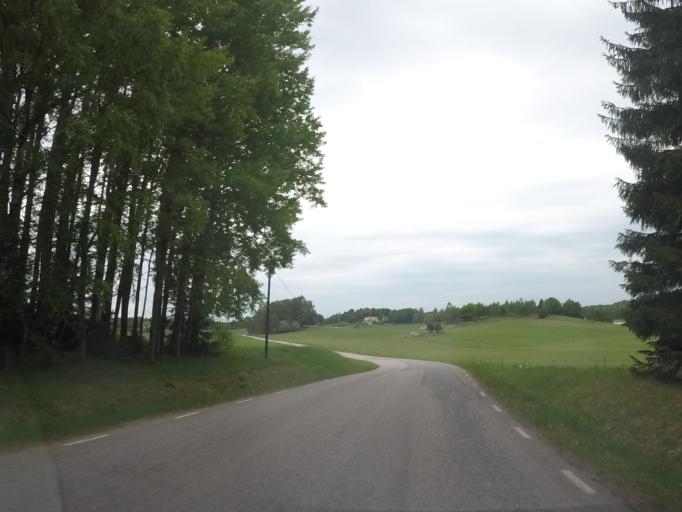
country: SE
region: Soedermanland
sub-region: Nykopings Kommun
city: Stigtomta
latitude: 58.9133
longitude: 16.8803
